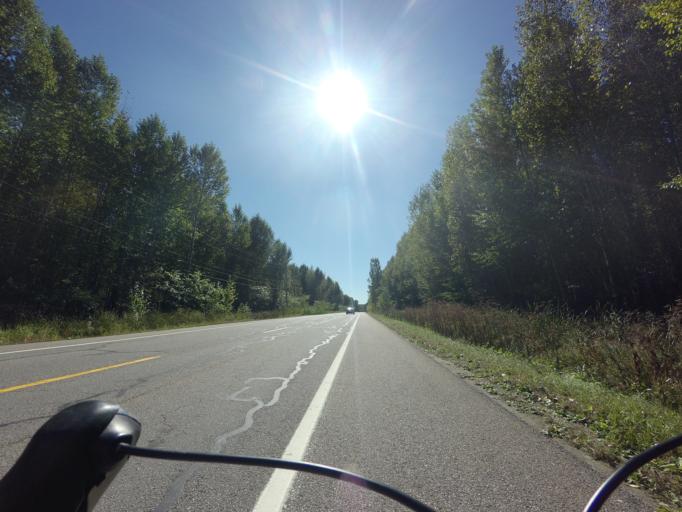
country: CA
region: Ontario
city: Clarence-Rockland
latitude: 45.5360
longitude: -75.4136
